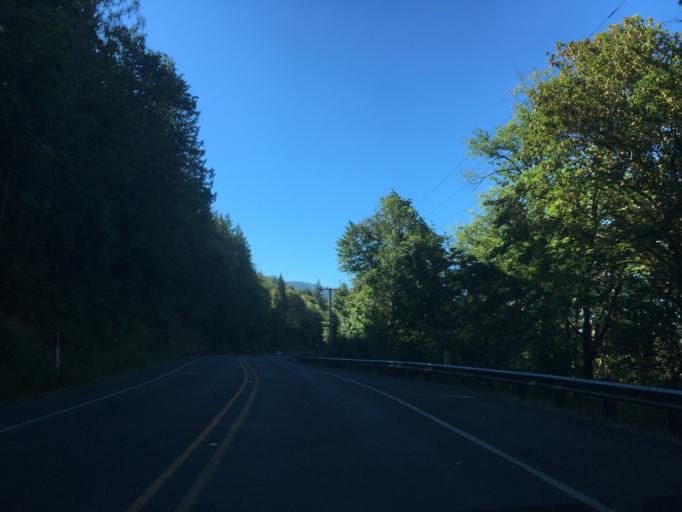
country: US
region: Washington
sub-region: Whatcom County
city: Sudden Valley
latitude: 48.6999
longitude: -122.1966
